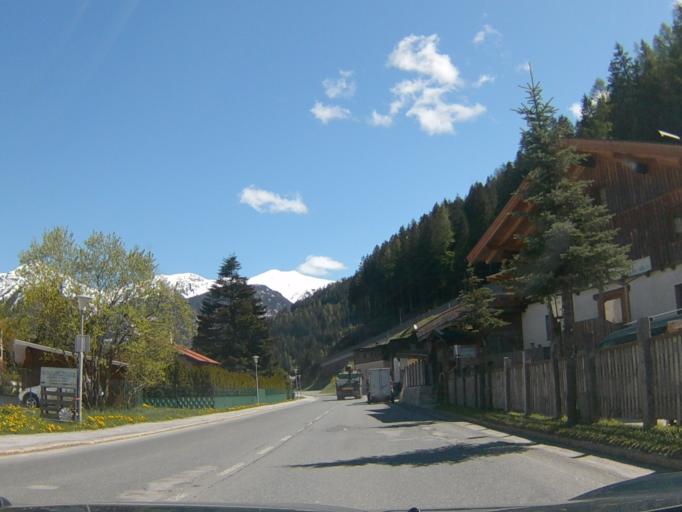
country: AT
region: Salzburg
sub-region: Politischer Bezirk Sankt Johann im Pongau
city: Bad Gastein
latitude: 47.1015
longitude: 13.1283
